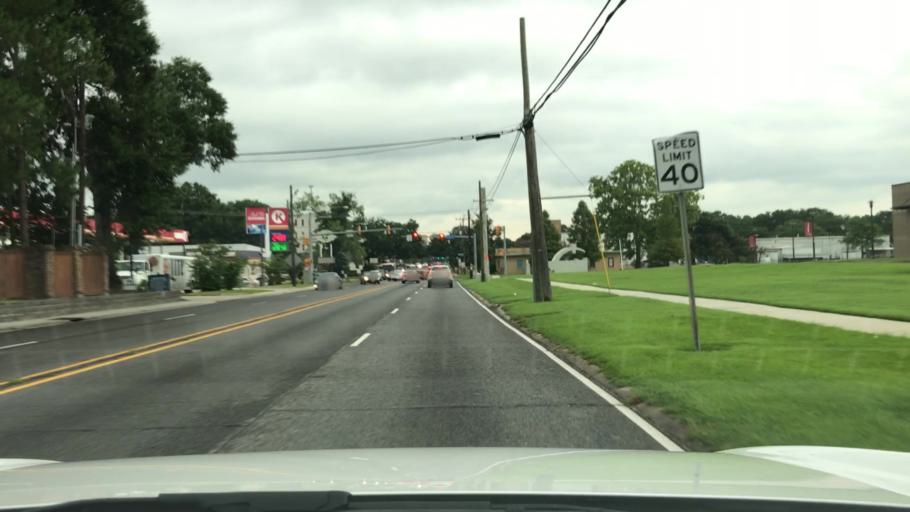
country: US
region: Louisiana
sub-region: East Baton Rouge Parish
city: Baton Rouge
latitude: 30.4477
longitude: -91.1388
